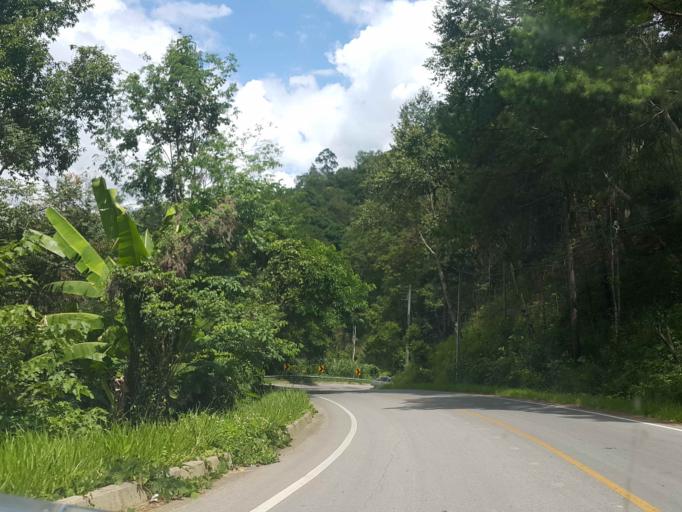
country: TH
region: Chiang Mai
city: Samoeng
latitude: 18.8781
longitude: 98.7888
